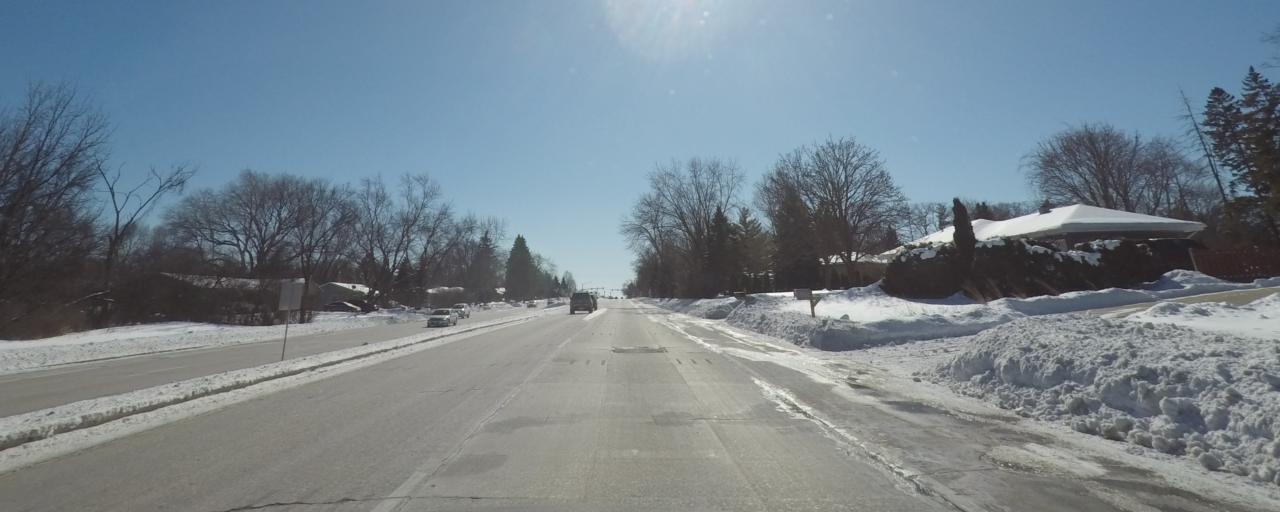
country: US
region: Wisconsin
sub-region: Waukesha County
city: New Berlin
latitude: 42.9851
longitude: -88.1084
